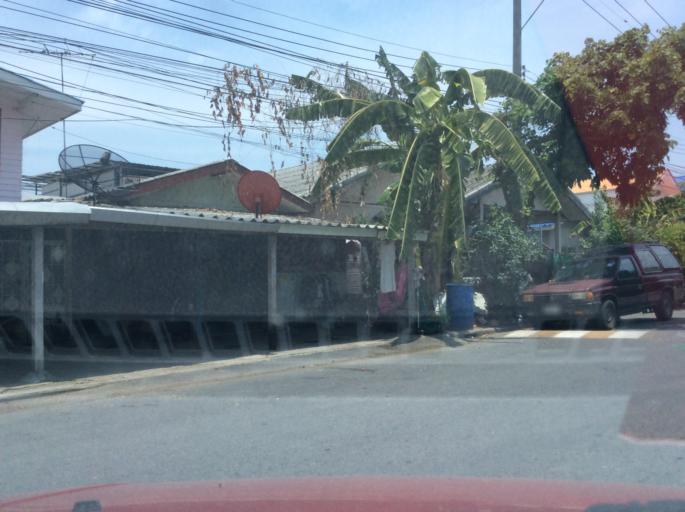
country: TH
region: Pathum Thani
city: Lam Luk Ka
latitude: 13.9482
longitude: 100.7358
